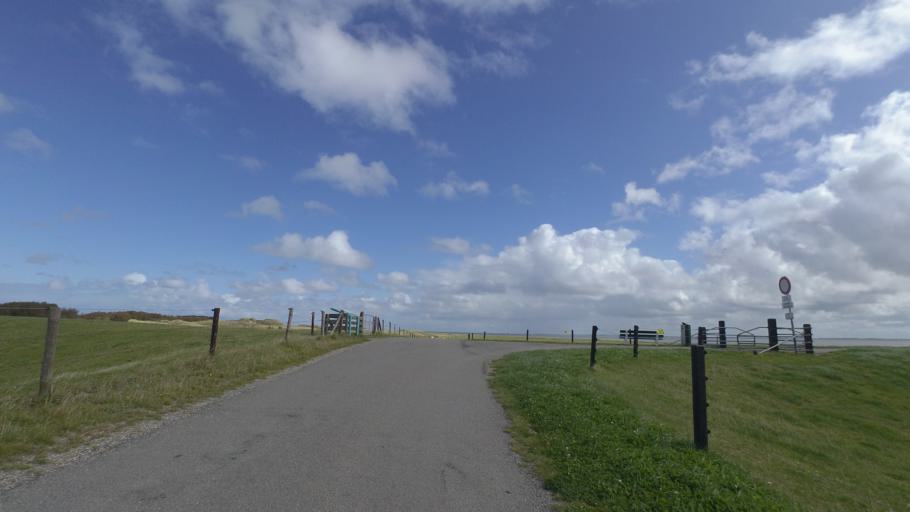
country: NL
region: Friesland
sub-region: Gemeente Ameland
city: Nes
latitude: 53.4474
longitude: 5.8497
